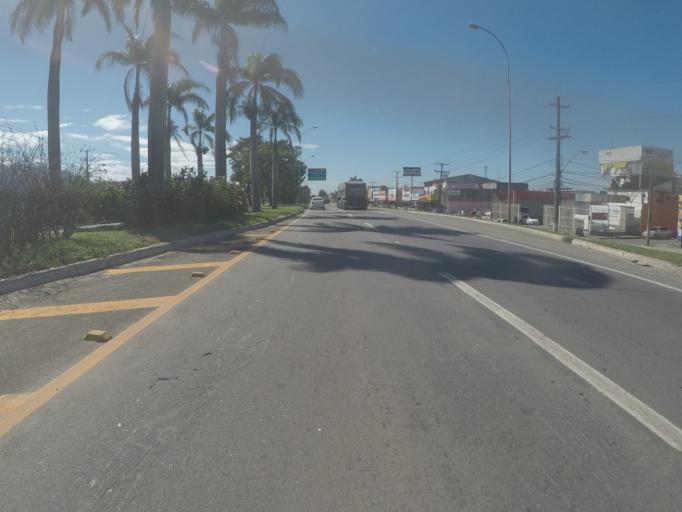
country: BR
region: Espirito Santo
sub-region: Serra
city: Serra
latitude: -20.2203
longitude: -40.2702
